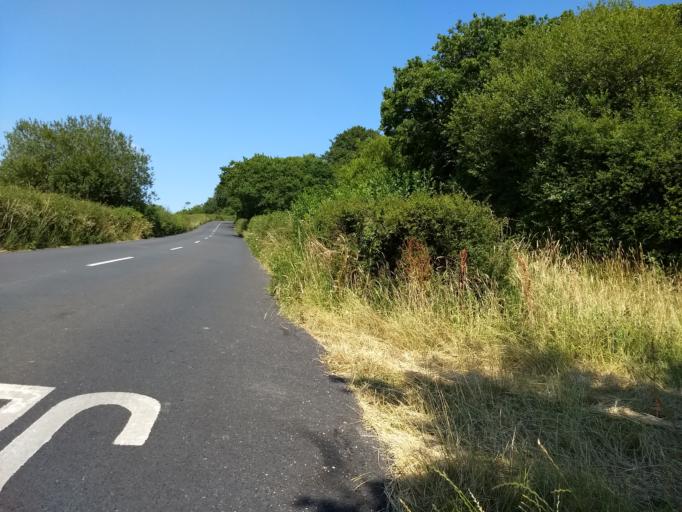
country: GB
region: England
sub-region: Isle of Wight
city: Northwood
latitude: 50.7222
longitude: -1.3629
